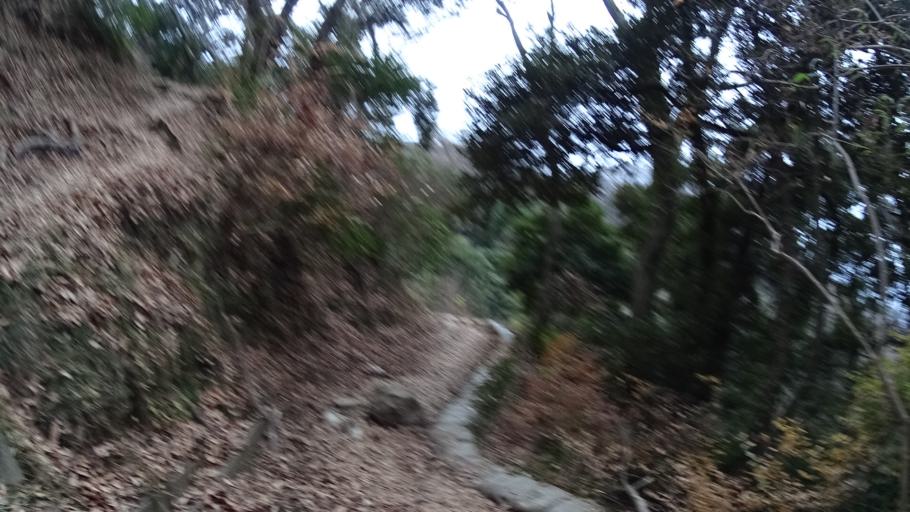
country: JP
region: Kanagawa
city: Oiso
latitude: 35.3177
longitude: 139.3087
